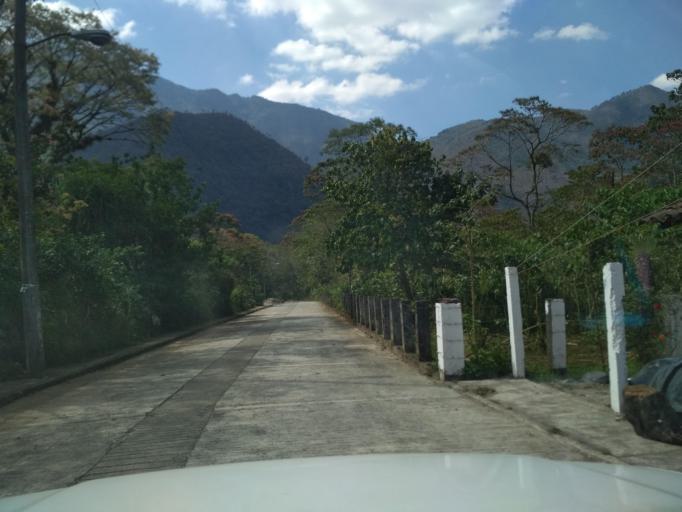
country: MX
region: Veracruz
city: Jalapilla
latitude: 18.7905
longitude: -97.0991
